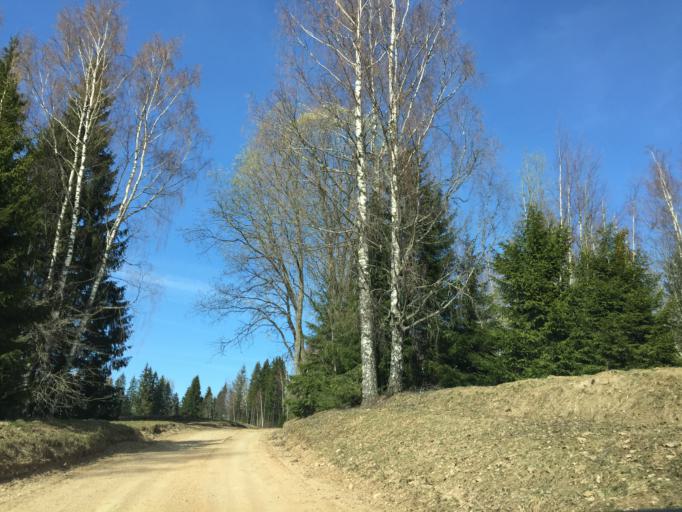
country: EE
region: Vorumaa
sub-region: Antsla vald
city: Vana-Antsla
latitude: 57.9781
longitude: 26.3536
